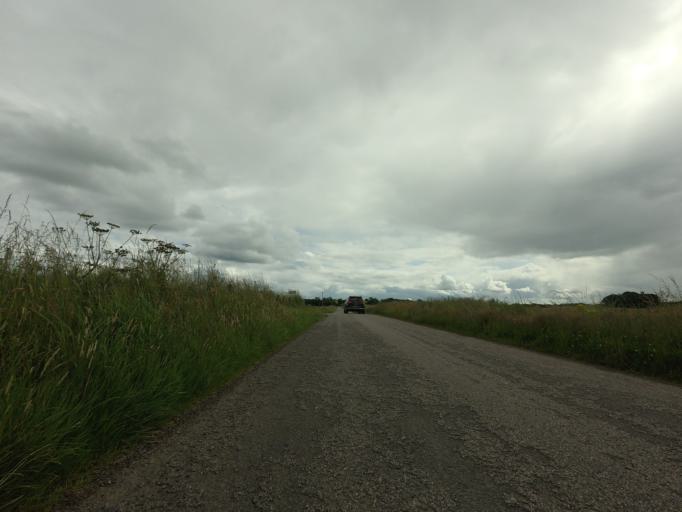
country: GB
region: Scotland
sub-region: Moray
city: Lhanbryd
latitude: 57.6576
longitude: -3.2096
